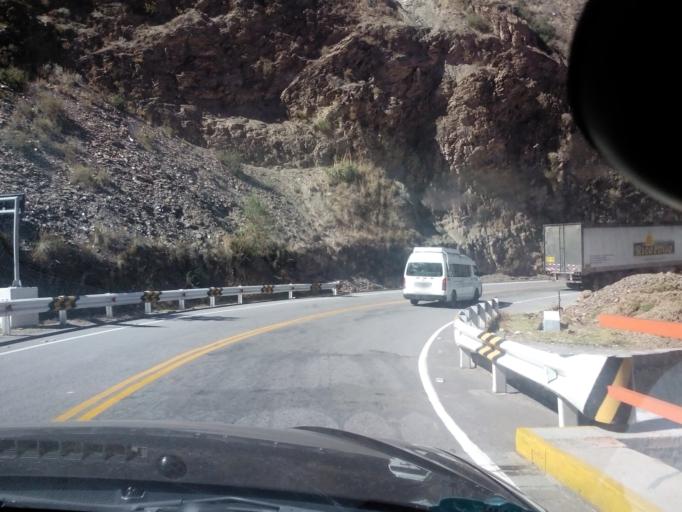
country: PE
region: Cusco
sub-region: Provincia de Quispicanchis
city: Urcos
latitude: -13.6869
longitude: -71.5936
